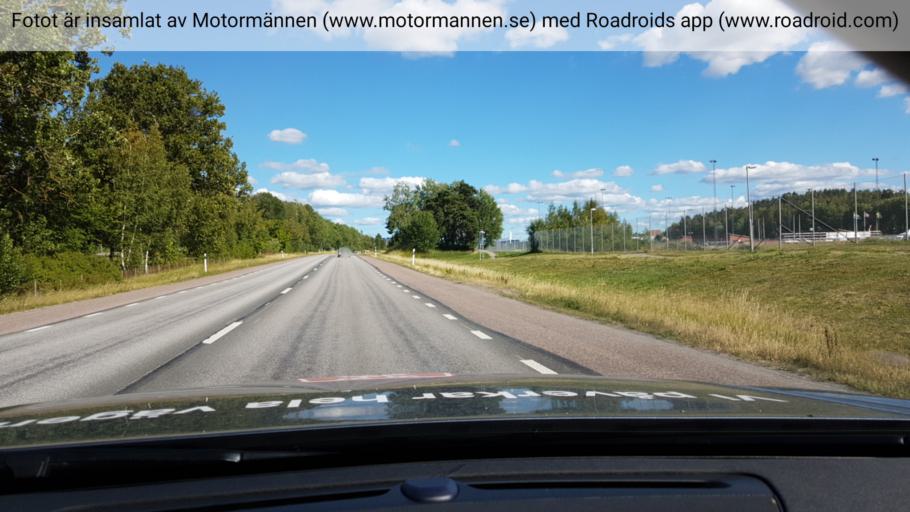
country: SE
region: Stockholm
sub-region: Sigtuna Kommun
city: Marsta
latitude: 59.6250
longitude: 17.8282
